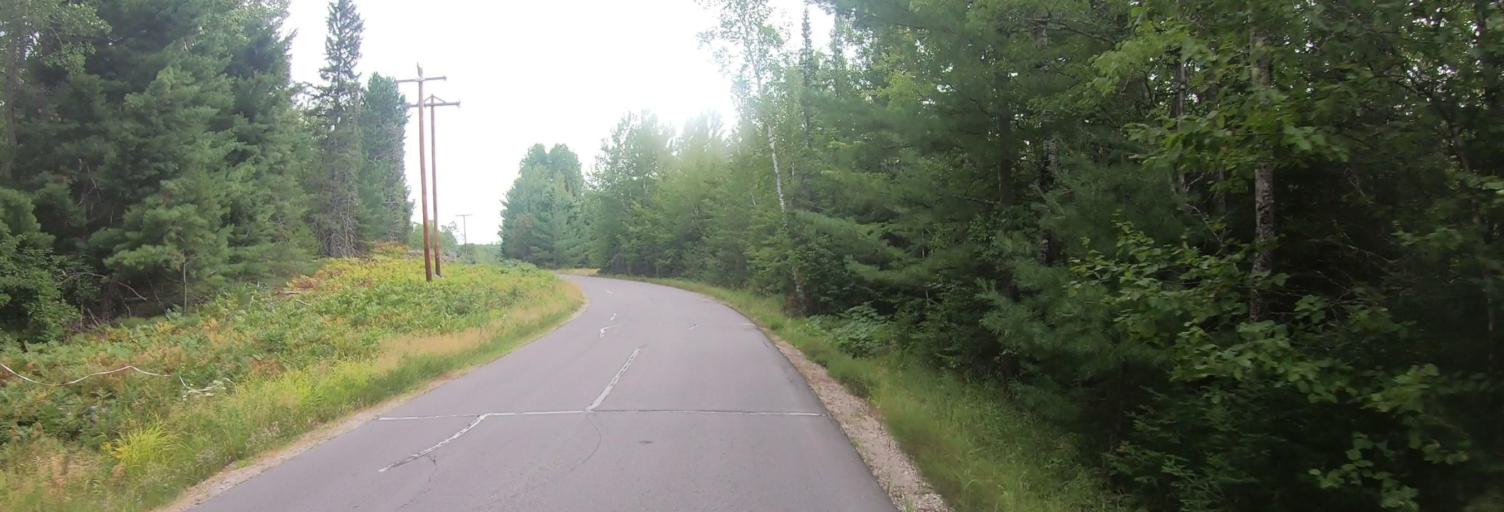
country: US
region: Minnesota
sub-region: Saint Louis County
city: Mountain Iron
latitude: 47.9523
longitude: -92.6595
